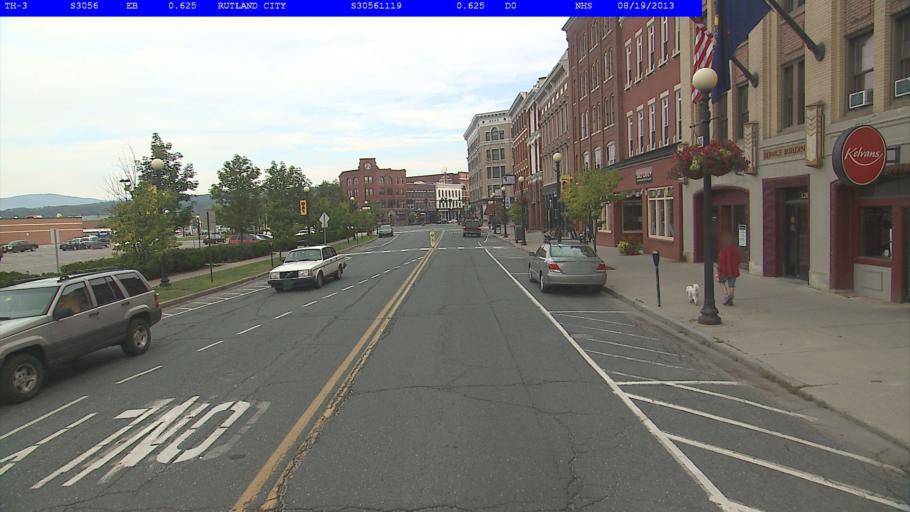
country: US
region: Vermont
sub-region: Rutland County
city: Rutland
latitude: 43.6057
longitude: -72.9789
